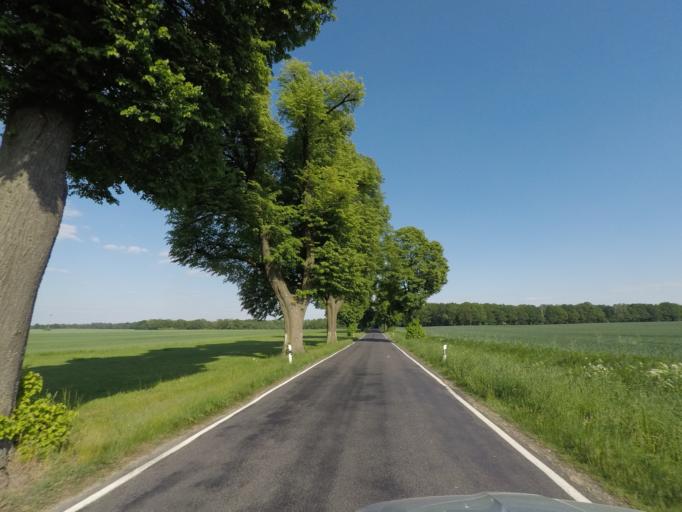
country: DE
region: Brandenburg
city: Hohenfinow
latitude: 52.7254
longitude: 13.8805
